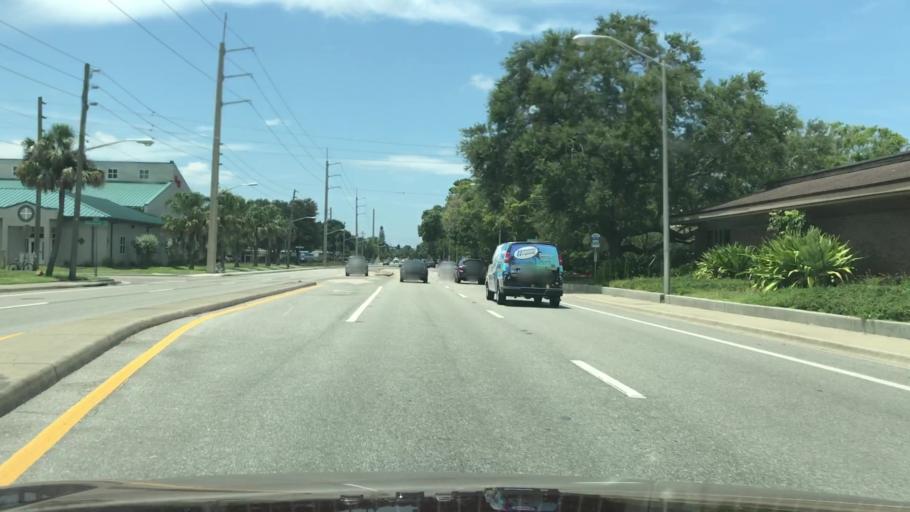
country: US
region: Florida
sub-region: Sarasota County
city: Southgate
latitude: 27.3184
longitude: -82.5141
